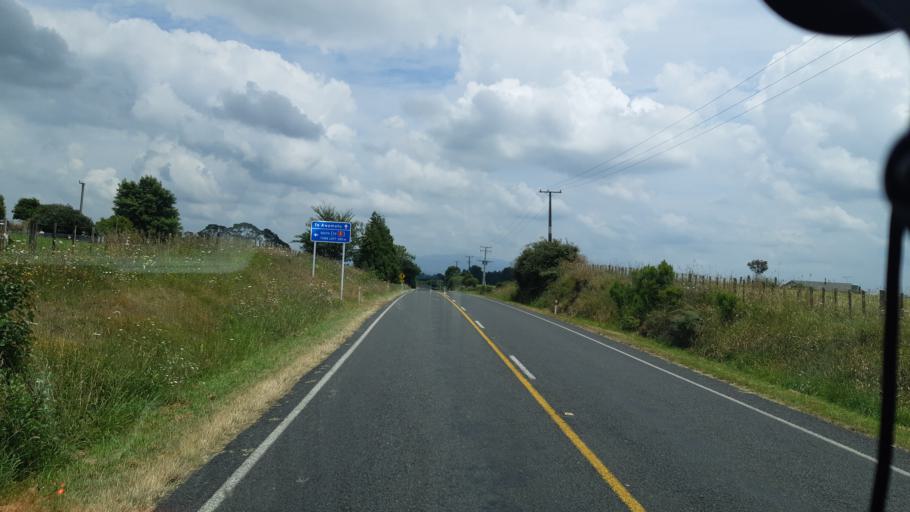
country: NZ
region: Waikato
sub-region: Waipa District
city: Cambridge
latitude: -38.0515
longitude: 175.3814
